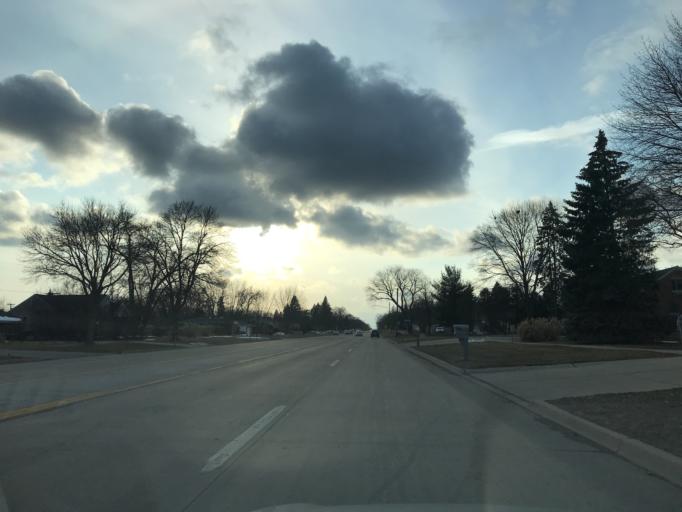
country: US
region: Michigan
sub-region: Oakland County
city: Farmington
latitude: 42.4269
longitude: -83.3441
